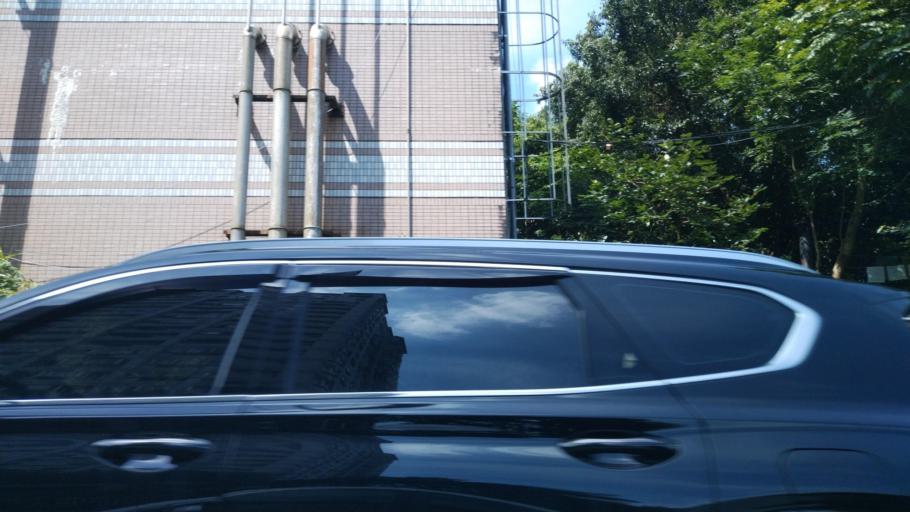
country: TW
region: Taipei
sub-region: Taipei
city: Banqiao
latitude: 24.9384
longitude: 121.5023
